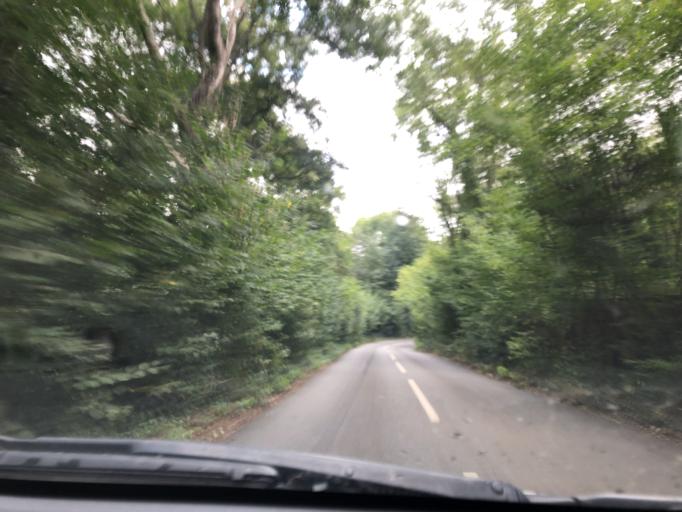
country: GB
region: England
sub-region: Kent
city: Westerham
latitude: 51.2395
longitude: 0.0848
